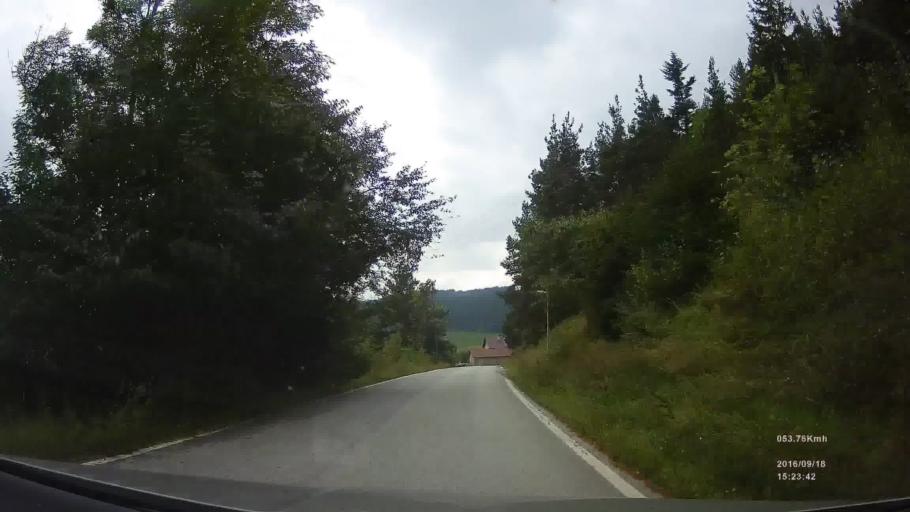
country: SK
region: Presovsky
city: Lubica
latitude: 49.0390
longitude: 20.4903
